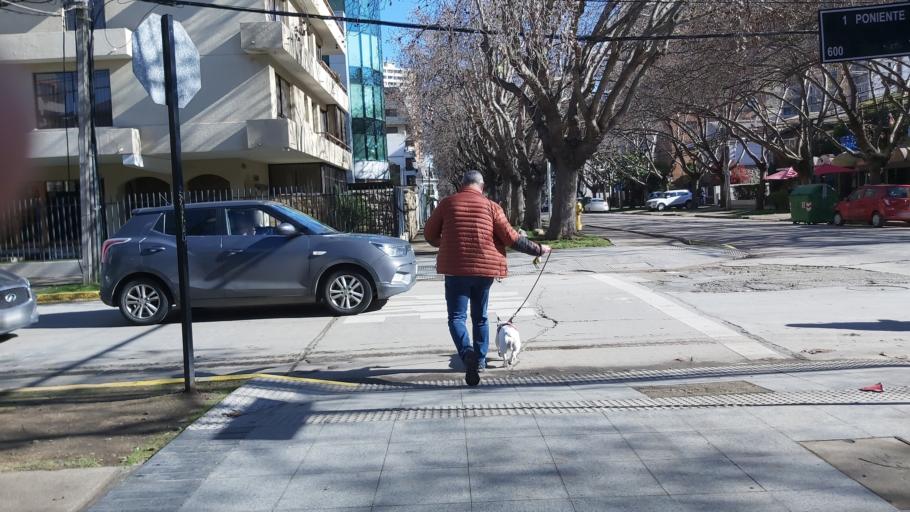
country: CL
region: Valparaiso
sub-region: Provincia de Valparaiso
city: Vina del Mar
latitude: -33.0152
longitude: -71.5512
